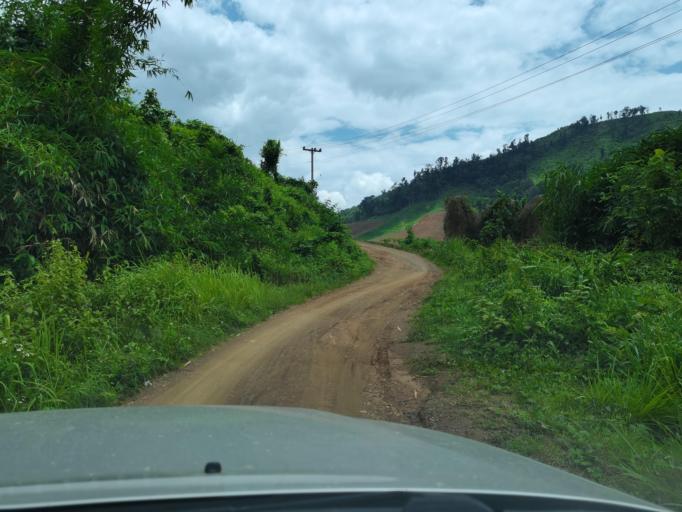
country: LA
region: Loungnamtha
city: Muang Long
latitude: 20.7330
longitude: 101.0145
